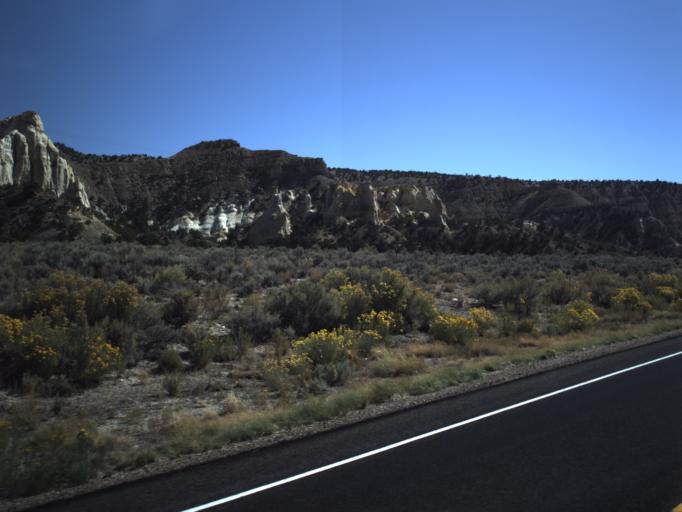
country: US
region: Utah
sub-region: Garfield County
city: Panguitch
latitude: 37.5785
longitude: -111.9861
